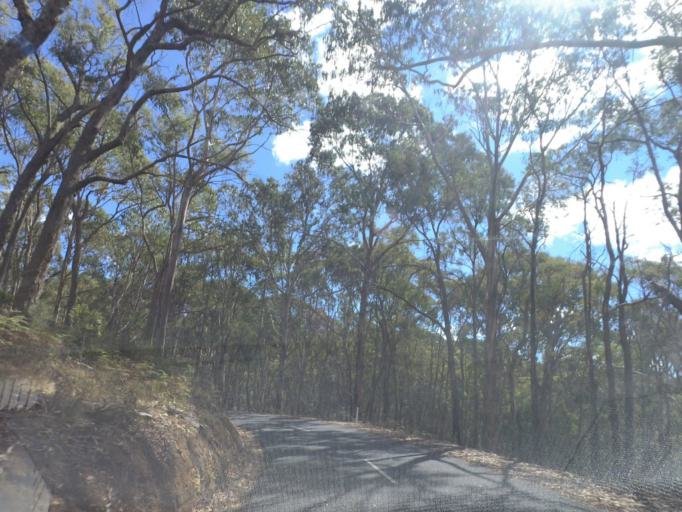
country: AU
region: Victoria
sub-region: Murrindindi
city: Alexandra
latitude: -37.3369
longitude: 145.9639
